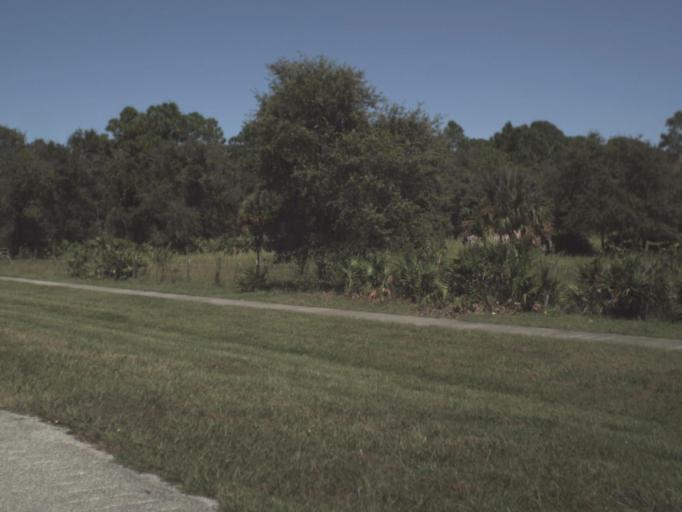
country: US
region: Florida
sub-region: Lee County
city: San Carlos Park
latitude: 26.4728
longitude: -81.8358
